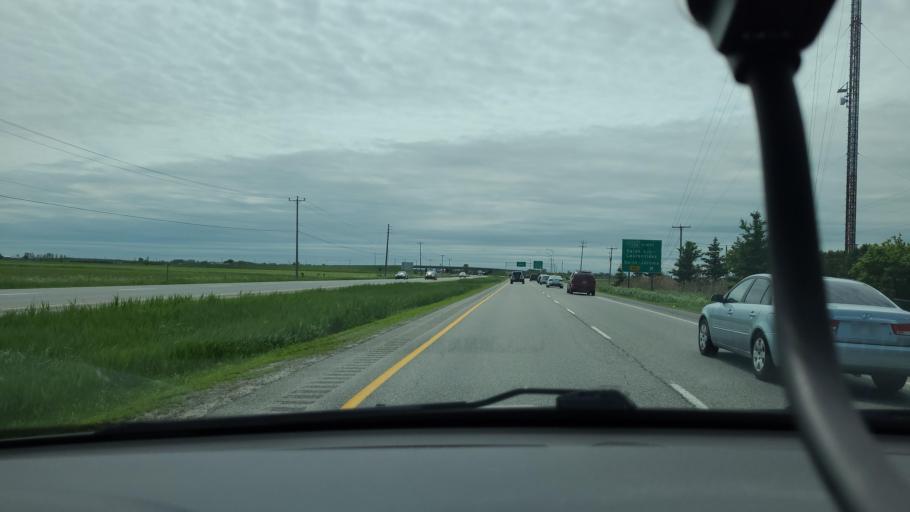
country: CA
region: Quebec
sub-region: Lanaudiere
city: Sainte-Julienne
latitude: 45.8912
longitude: -73.6606
